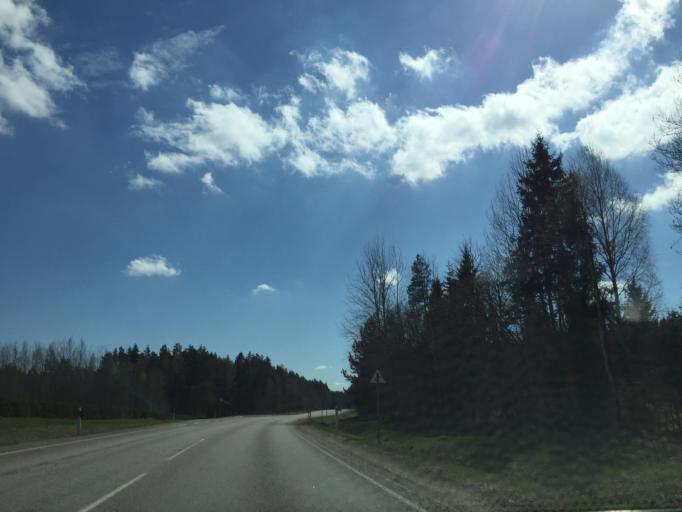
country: EE
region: Valgamaa
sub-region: Torva linn
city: Torva
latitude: 58.0135
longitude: 26.1631
